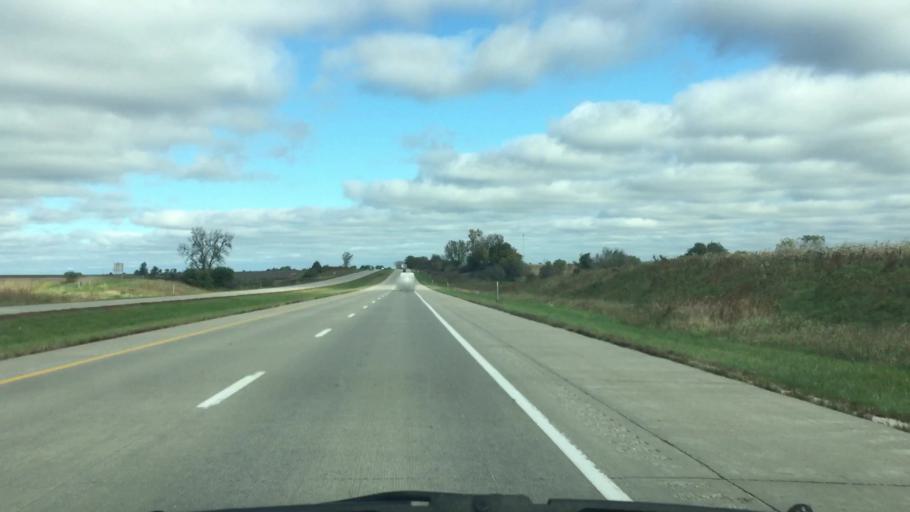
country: US
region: Iowa
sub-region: Clarke County
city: Osceola
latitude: 40.9195
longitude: -93.7969
